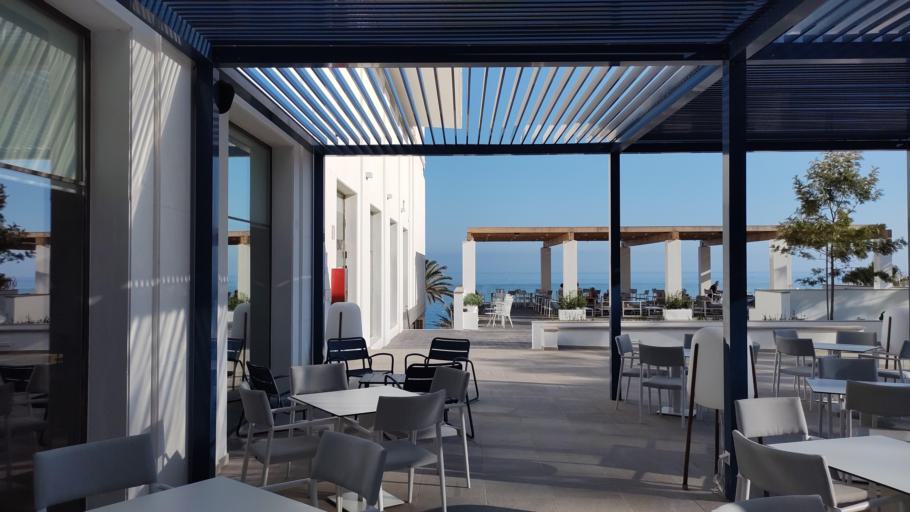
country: ES
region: Andalusia
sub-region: Provincia de Malaga
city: Benalmadena
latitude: 36.5800
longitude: -4.5427
